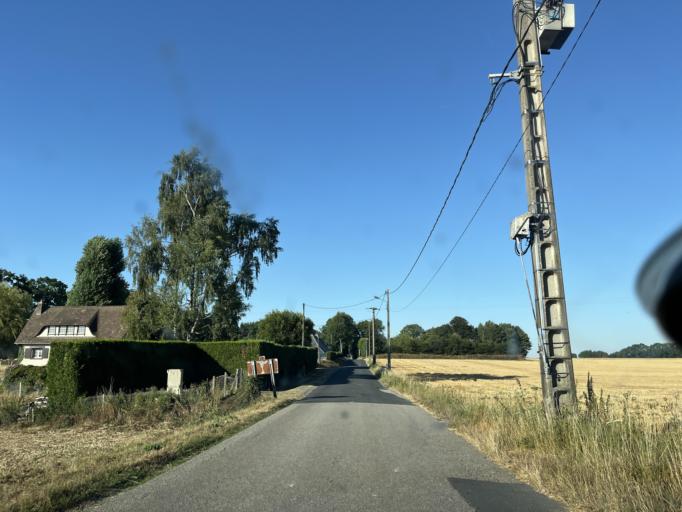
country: FR
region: Haute-Normandie
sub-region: Departement de la Seine-Maritime
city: Lanquetot
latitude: 49.5718
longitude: 0.5980
